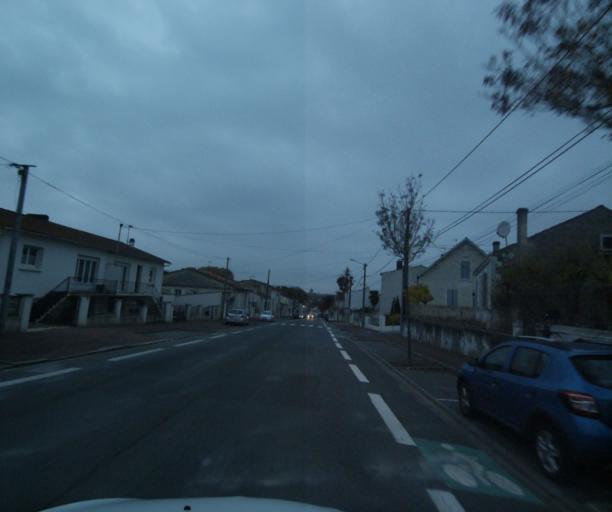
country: FR
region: Poitou-Charentes
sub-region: Departement de la Charente-Maritime
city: Saintes
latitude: 45.7454
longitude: -0.6097
